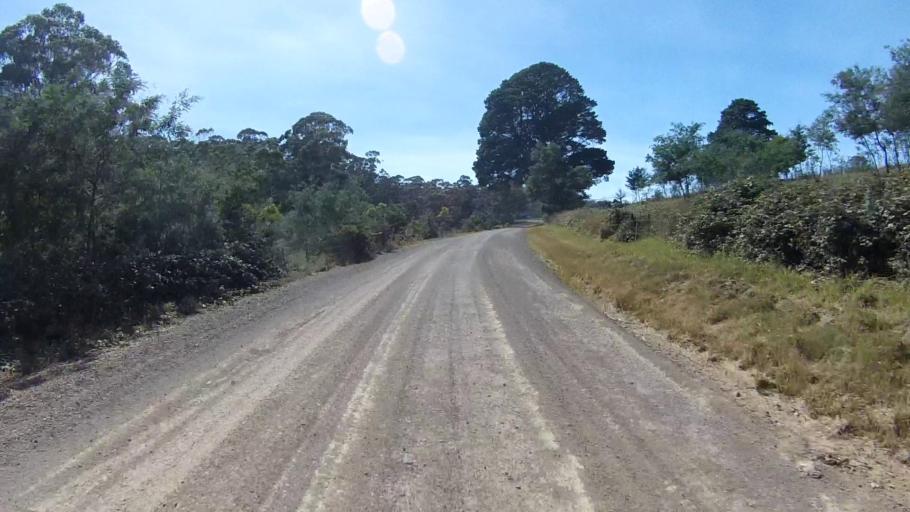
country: AU
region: Tasmania
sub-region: Sorell
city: Sorell
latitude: -42.7557
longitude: 147.6645
